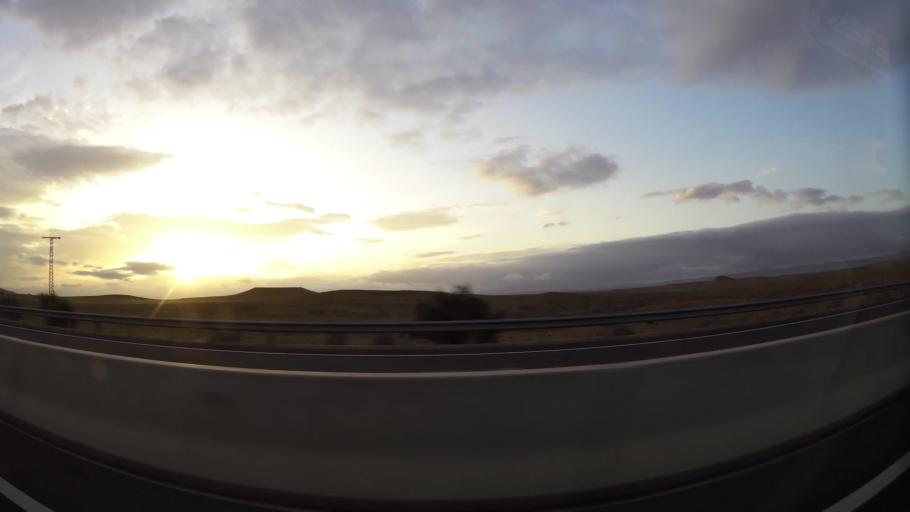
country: MA
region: Oriental
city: Taourirt
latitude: 34.5275
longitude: -2.9253
